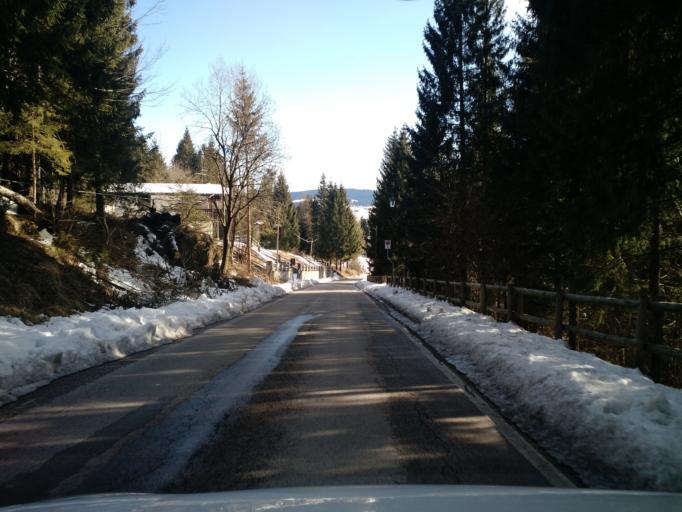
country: IT
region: Veneto
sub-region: Provincia di Vicenza
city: Roana
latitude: 45.8857
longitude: 11.4618
